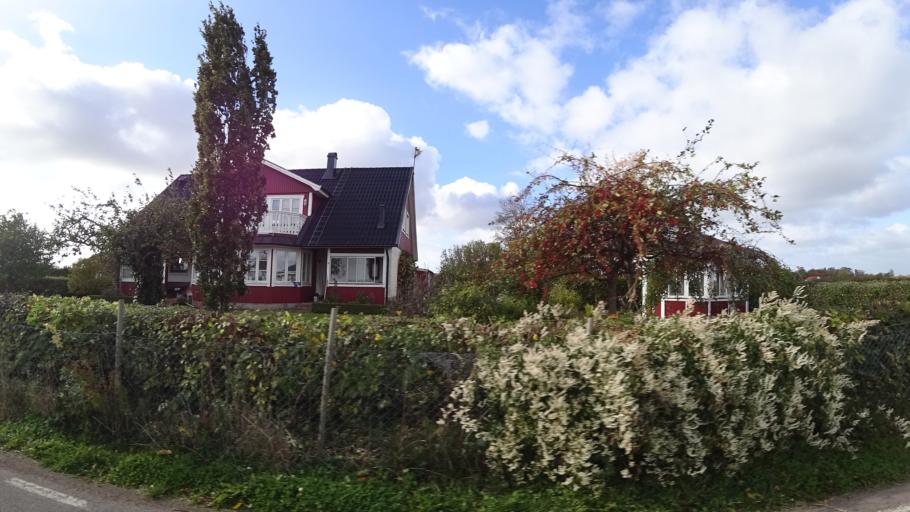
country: SE
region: Skane
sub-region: Staffanstorps Kommun
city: Hjaerup
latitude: 55.6507
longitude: 13.1701
